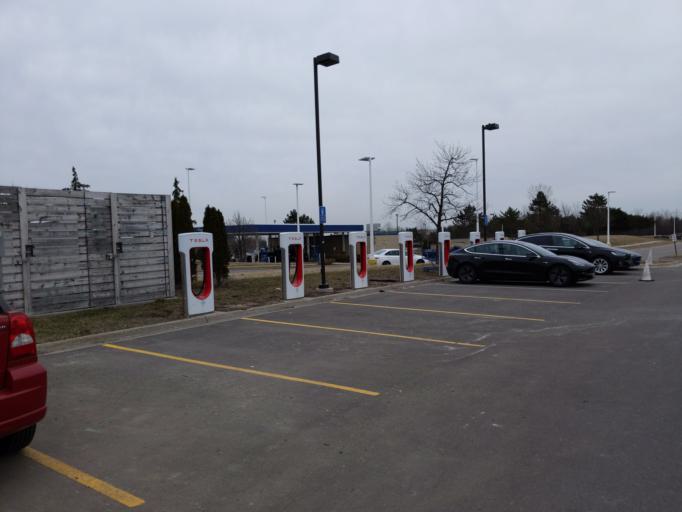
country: US
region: Michigan
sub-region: Washtenaw County
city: Ann Arbor
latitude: 42.2412
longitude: -83.7668
